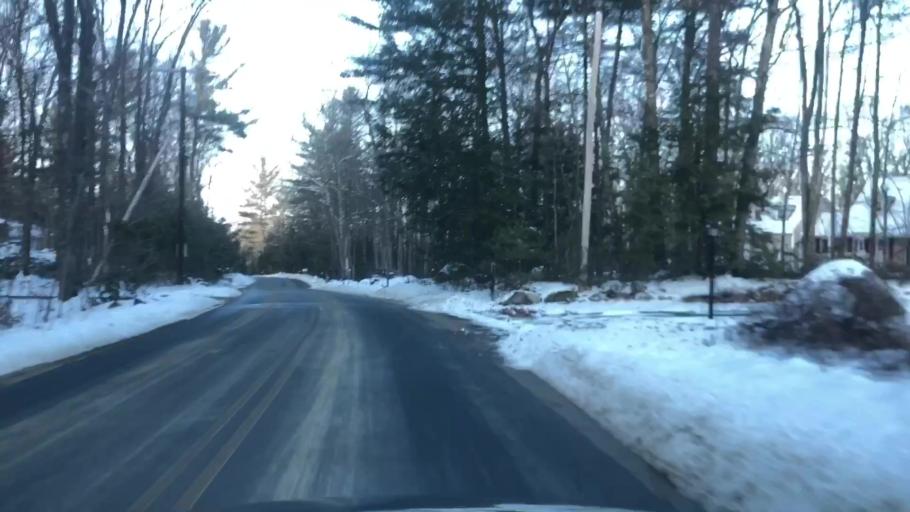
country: US
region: New Hampshire
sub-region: Hillsborough County
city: Milford
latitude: 42.8035
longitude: -71.6693
